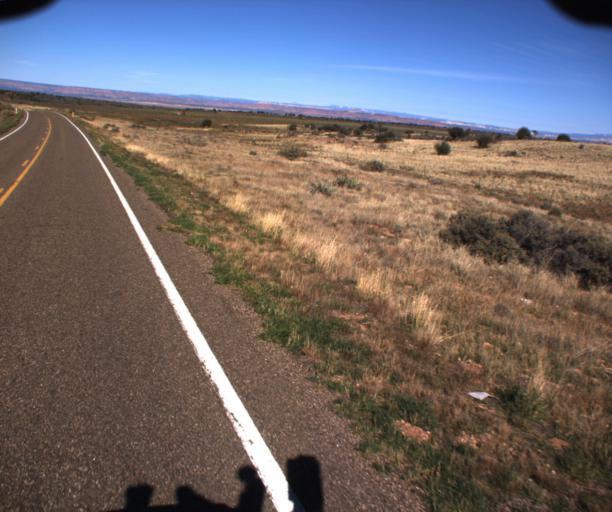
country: US
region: Arizona
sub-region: Coconino County
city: Fredonia
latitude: 36.8509
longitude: -112.2892
